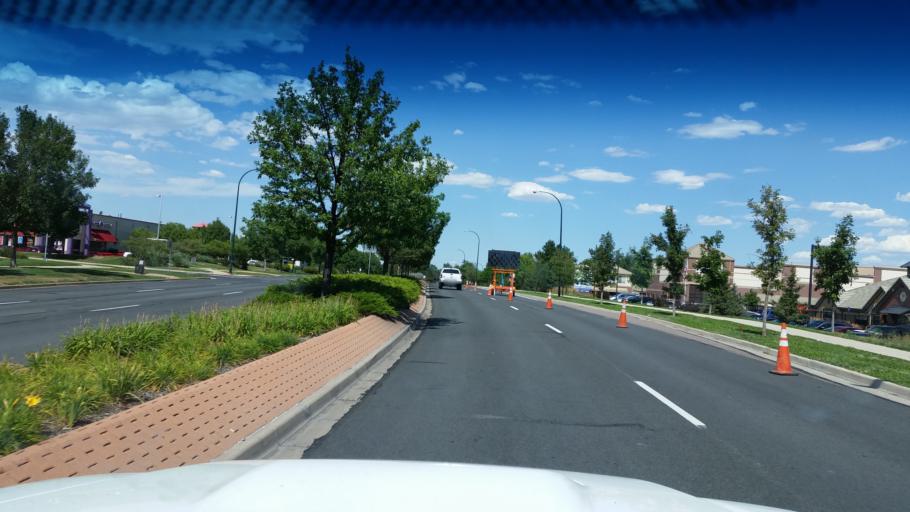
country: US
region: Colorado
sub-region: Broomfield County
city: Broomfield
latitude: 39.8787
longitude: -105.0924
